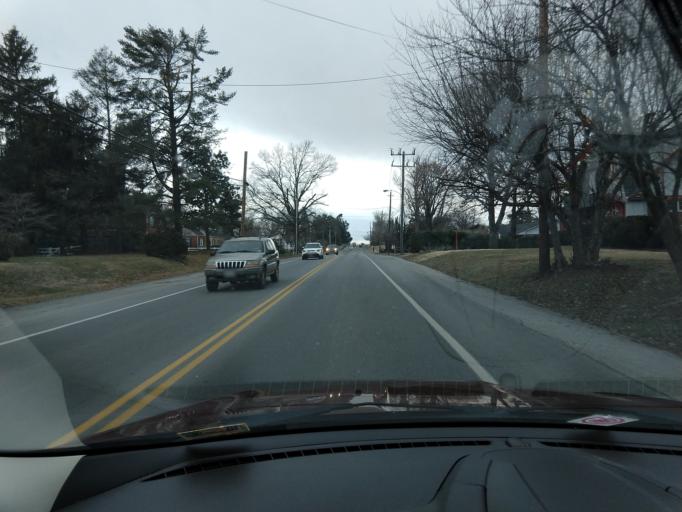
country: US
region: Virginia
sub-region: City of Waynesboro
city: Waynesboro
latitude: 38.0747
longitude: -78.9080
